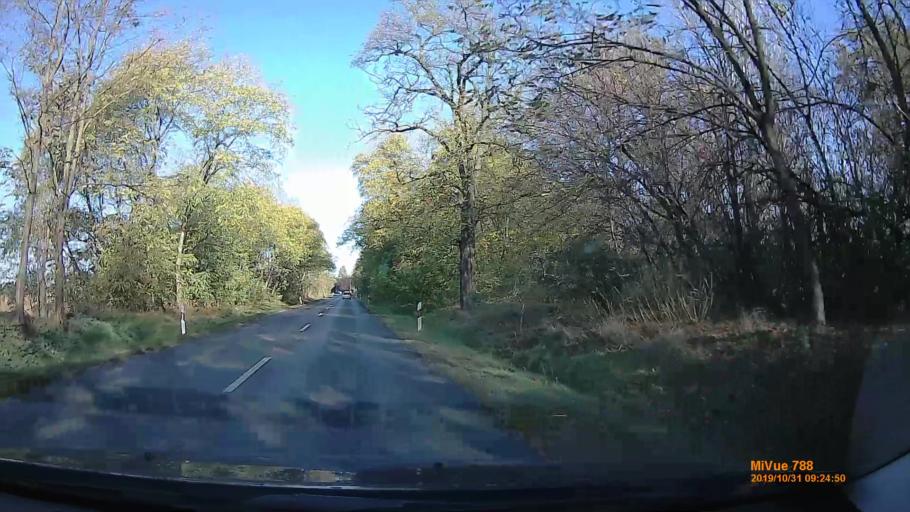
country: HU
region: Pest
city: Maglod
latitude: 47.4375
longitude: 19.3757
